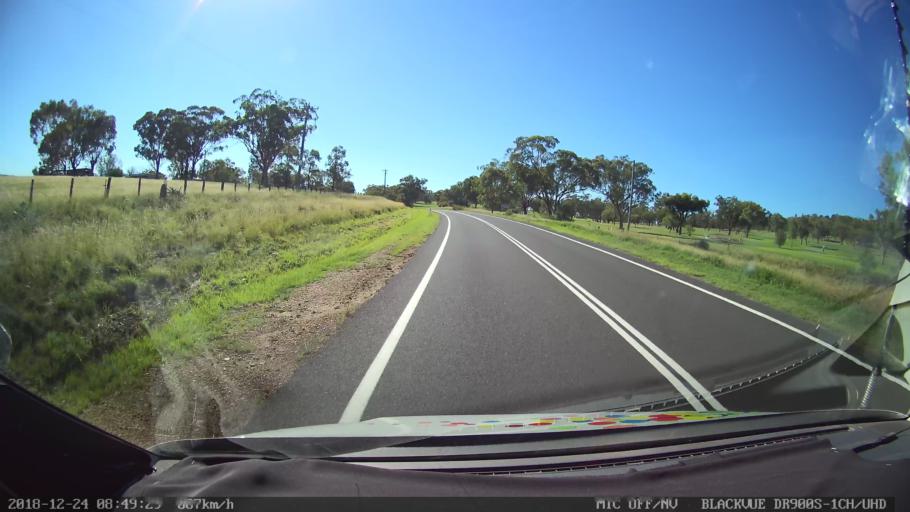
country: AU
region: New South Wales
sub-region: Liverpool Plains
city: Quirindi
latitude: -31.4676
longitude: 150.6546
